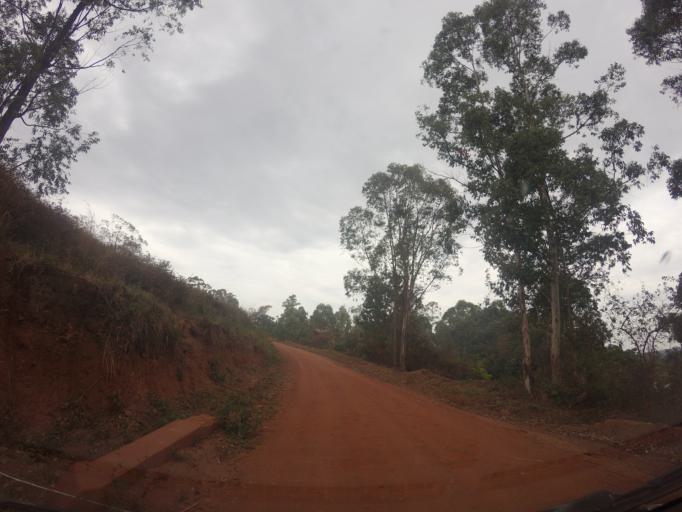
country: UG
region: Northern Region
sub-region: Zombo District
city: Zombo
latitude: 2.7659
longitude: 30.8578
